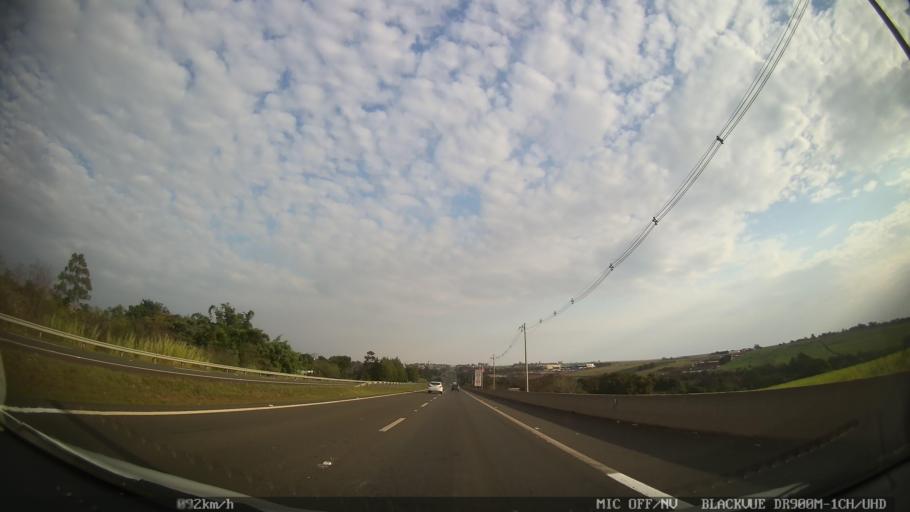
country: BR
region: Sao Paulo
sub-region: Cosmopolis
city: Cosmopolis
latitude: -22.6106
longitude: -47.1946
